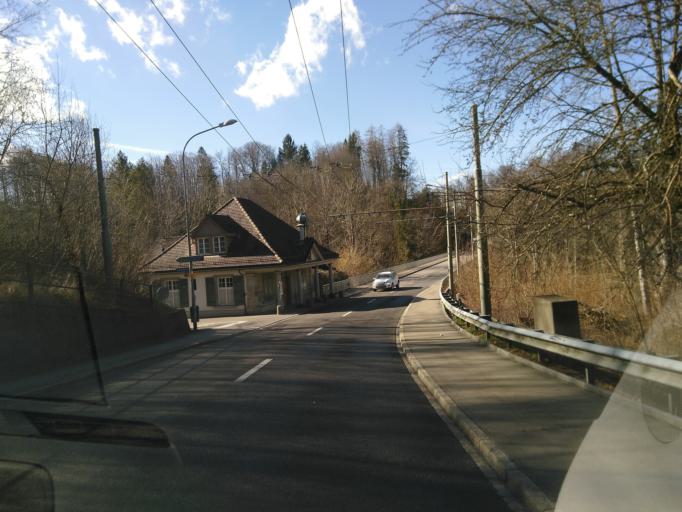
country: CH
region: Appenzell Ausserrhoden
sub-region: Bezirk Hinterland
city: Herisau
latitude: 47.4061
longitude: 9.3237
